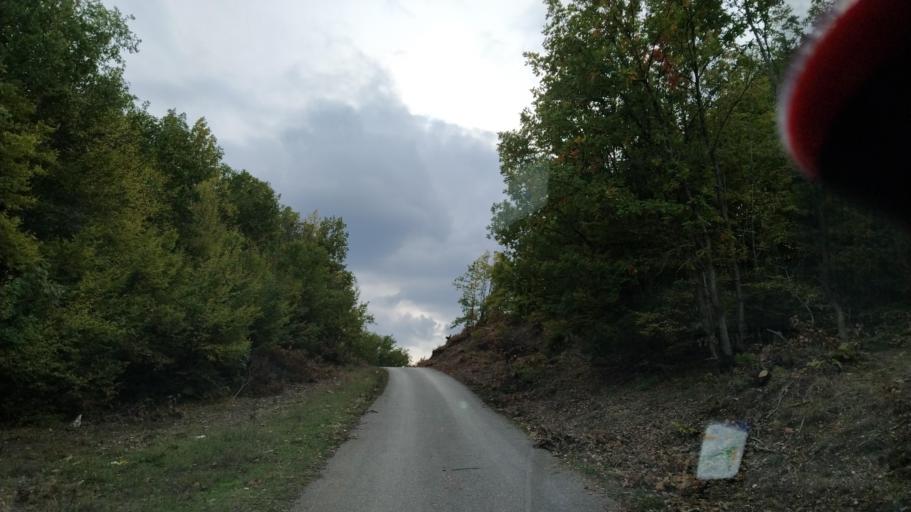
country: MK
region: Konce
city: Konce
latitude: 41.5069
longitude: 22.4622
